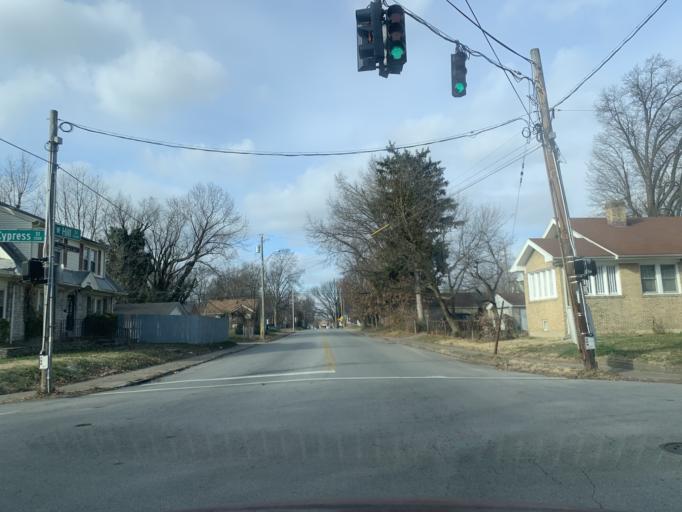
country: US
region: Kentucky
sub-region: Jefferson County
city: Shively
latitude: 38.2303
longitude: -85.7985
